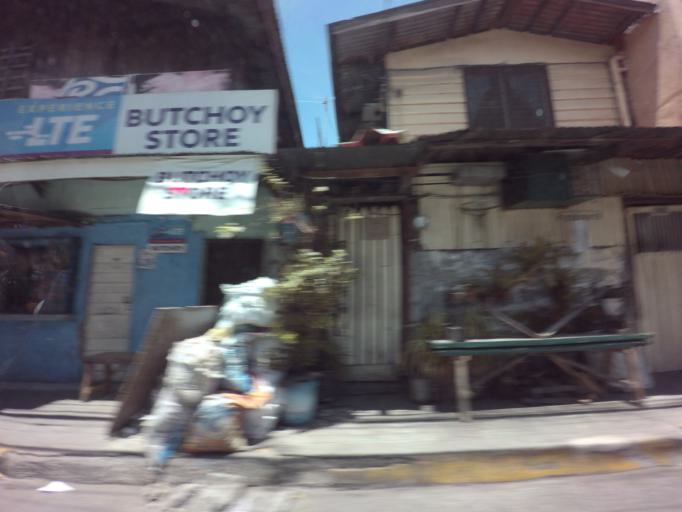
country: PH
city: Sambayanihan People's Village
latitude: 14.4905
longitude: 120.9891
